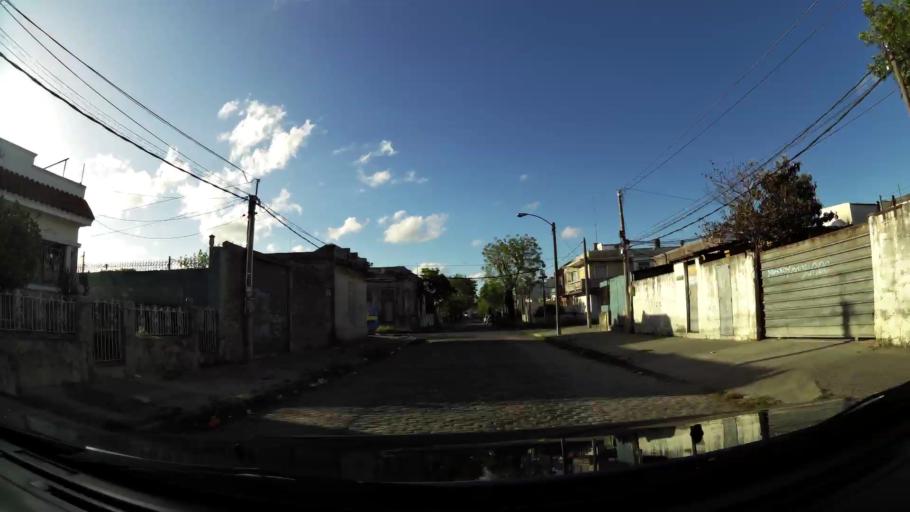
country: UY
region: Montevideo
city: Montevideo
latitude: -34.8689
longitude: -56.1475
